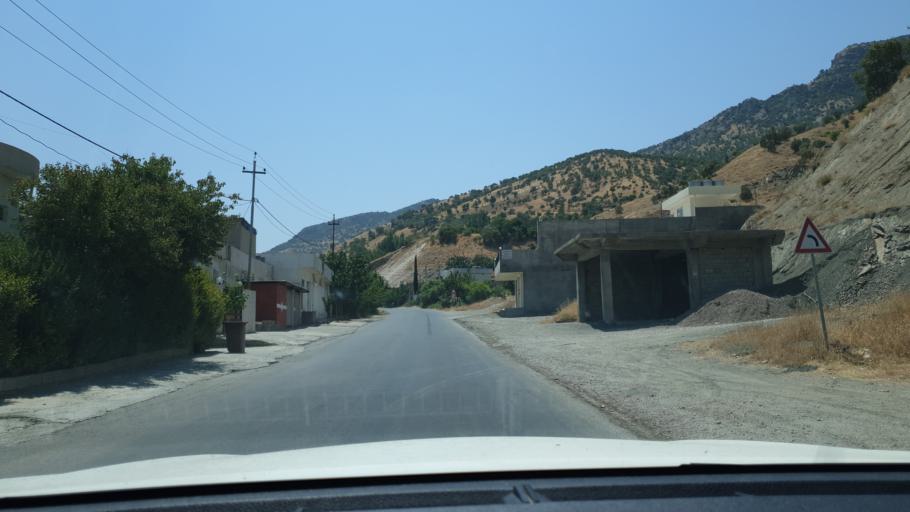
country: IQ
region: Arbil
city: Nahiyat Hiran
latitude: 36.2882
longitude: 44.4852
